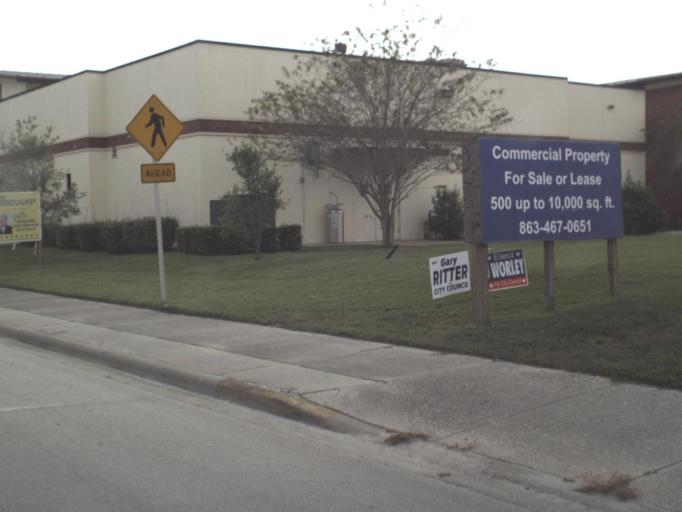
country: US
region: Florida
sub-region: Okeechobee County
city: Okeechobee
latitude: 27.2465
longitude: -80.8300
